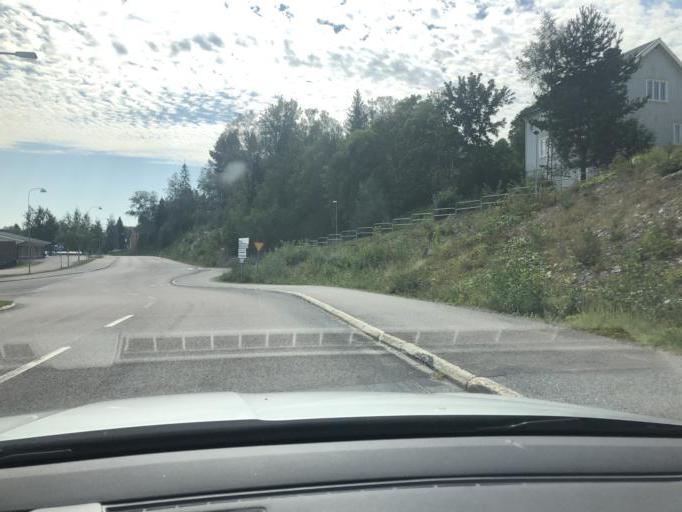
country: SE
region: Vaesternorrland
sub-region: Kramfors Kommun
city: Kramfors
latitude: 62.9280
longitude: 17.7785
